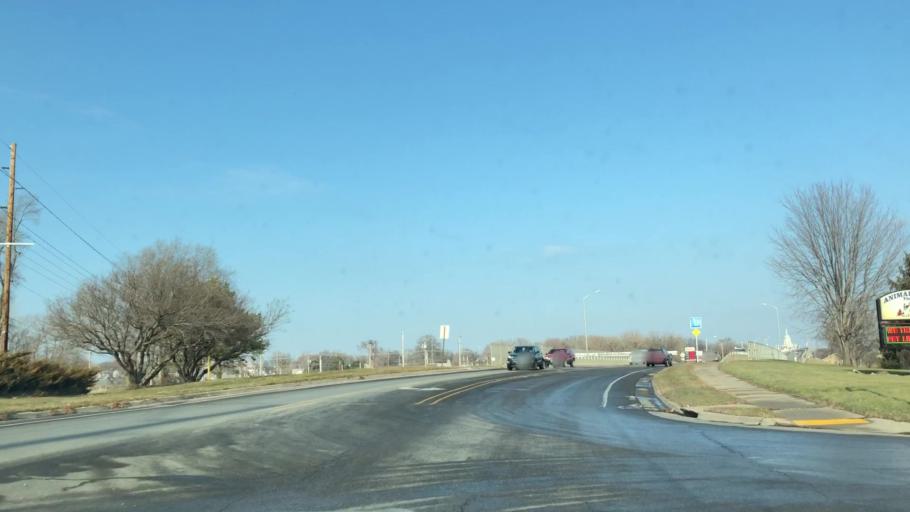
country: US
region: Iowa
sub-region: Marshall County
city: Marshalltown
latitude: 42.0364
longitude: -92.9222
